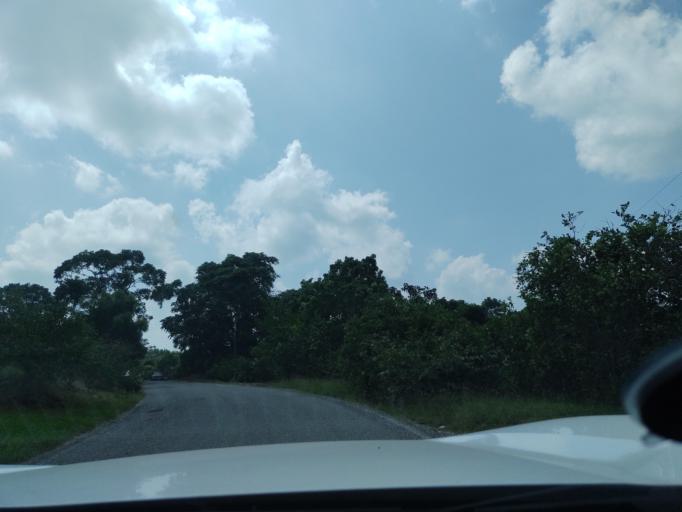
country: MX
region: Veracruz
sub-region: Martinez de la Torre
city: La Union Paso Largo
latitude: 20.1808
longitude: -97.0351
